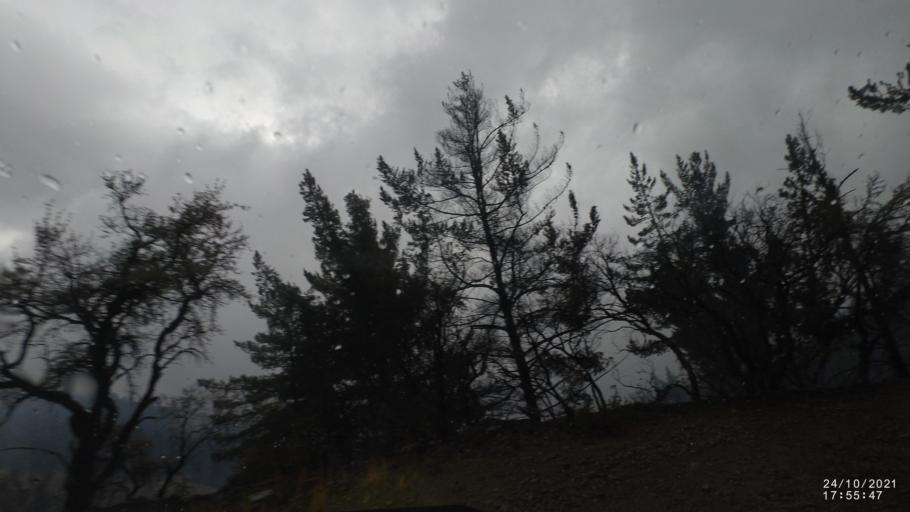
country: BO
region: Cochabamba
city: Cochabamba
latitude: -17.3227
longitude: -66.1277
